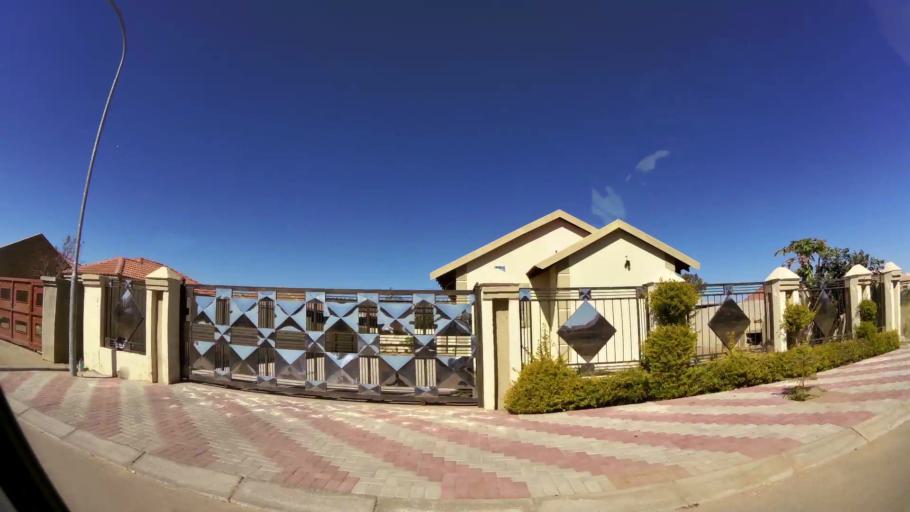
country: ZA
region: Limpopo
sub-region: Capricorn District Municipality
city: Polokwane
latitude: -23.8619
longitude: 29.4263
